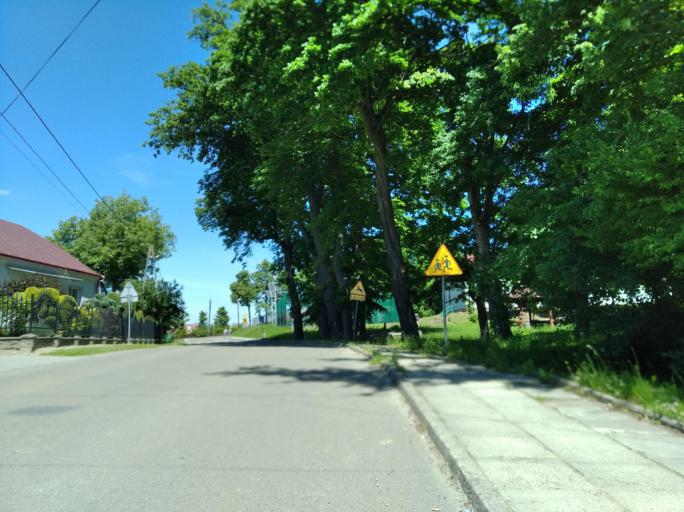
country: PL
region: Subcarpathian Voivodeship
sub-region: Powiat jasielski
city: Tarnowiec
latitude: 49.7301
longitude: 21.5767
